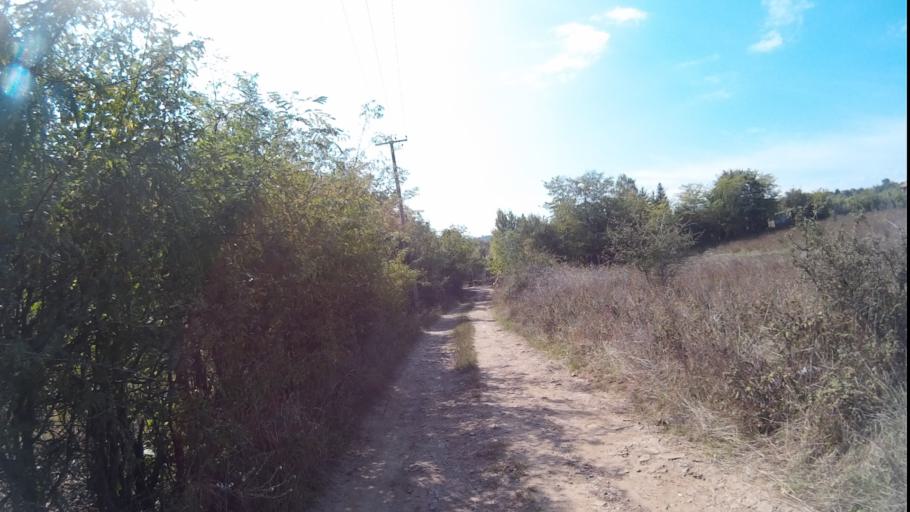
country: RS
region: Central Serbia
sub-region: Nisavski Okrug
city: Nis
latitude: 43.3006
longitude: 21.9124
